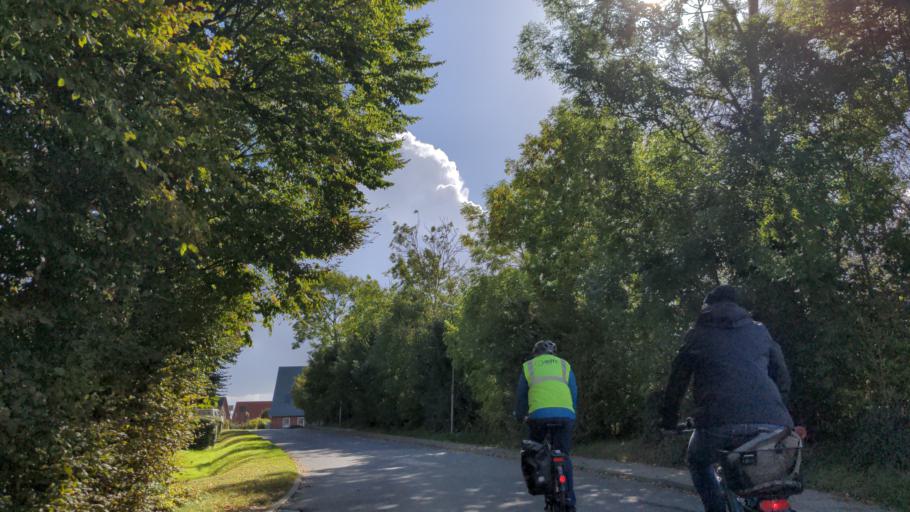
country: DE
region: Schleswig-Holstein
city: Reinfeld
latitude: 53.8282
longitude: 10.5081
